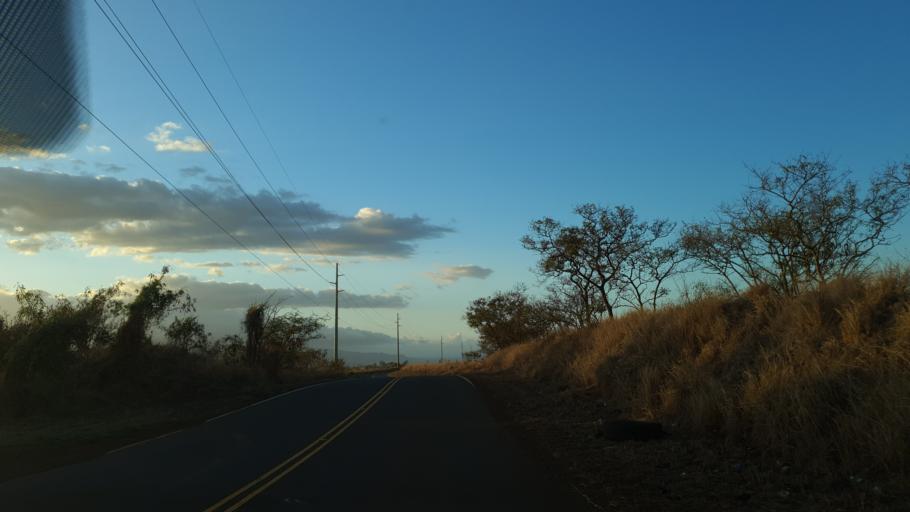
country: US
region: Hawaii
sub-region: Maui County
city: Pukalani
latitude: 20.8031
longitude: -156.3771
